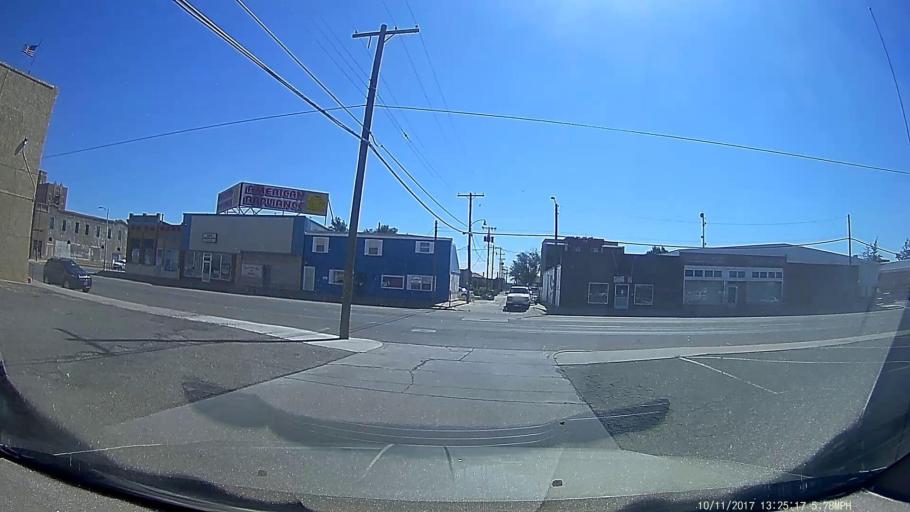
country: US
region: New Mexico
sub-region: Curry County
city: Clovis
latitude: 34.4010
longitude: -103.2083
